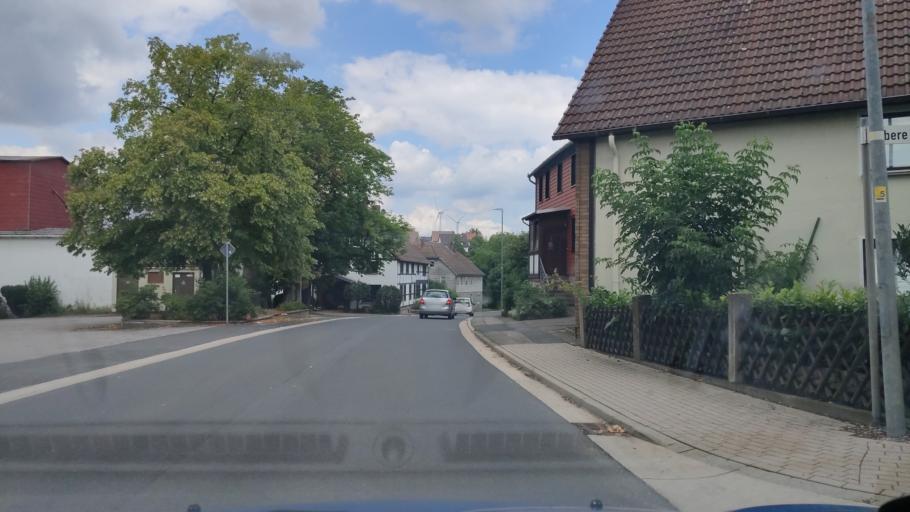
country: DE
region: Lower Saxony
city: Coppenbrugge
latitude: 52.1034
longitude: 9.5011
